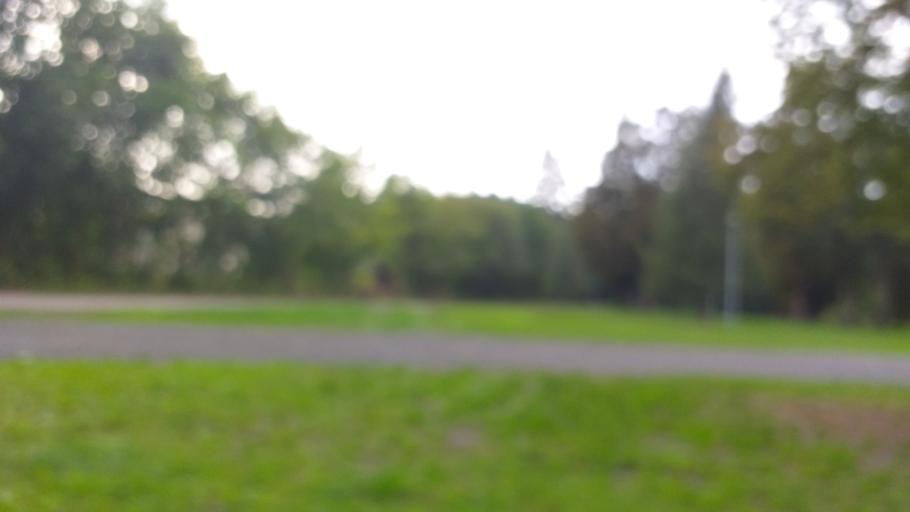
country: PL
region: Lower Silesian Voivodeship
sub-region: Powiat lubanski
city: Lesna
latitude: 51.0356
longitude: 15.2587
